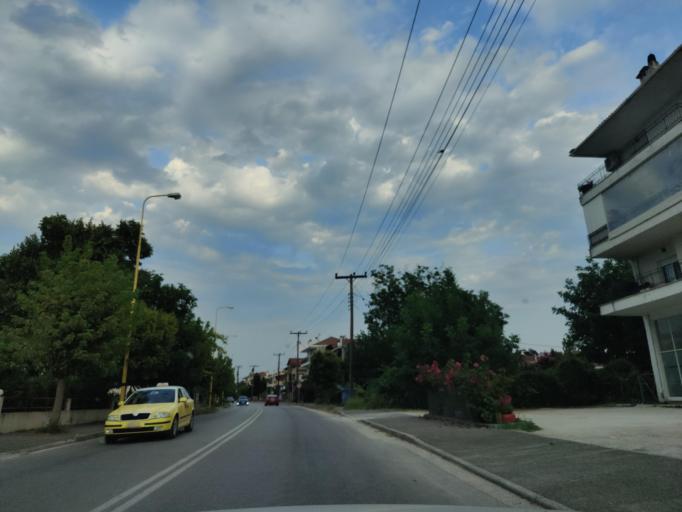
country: GR
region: East Macedonia and Thrace
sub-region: Nomos Dramas
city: Drama
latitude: 41.1540
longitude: 24.1148
